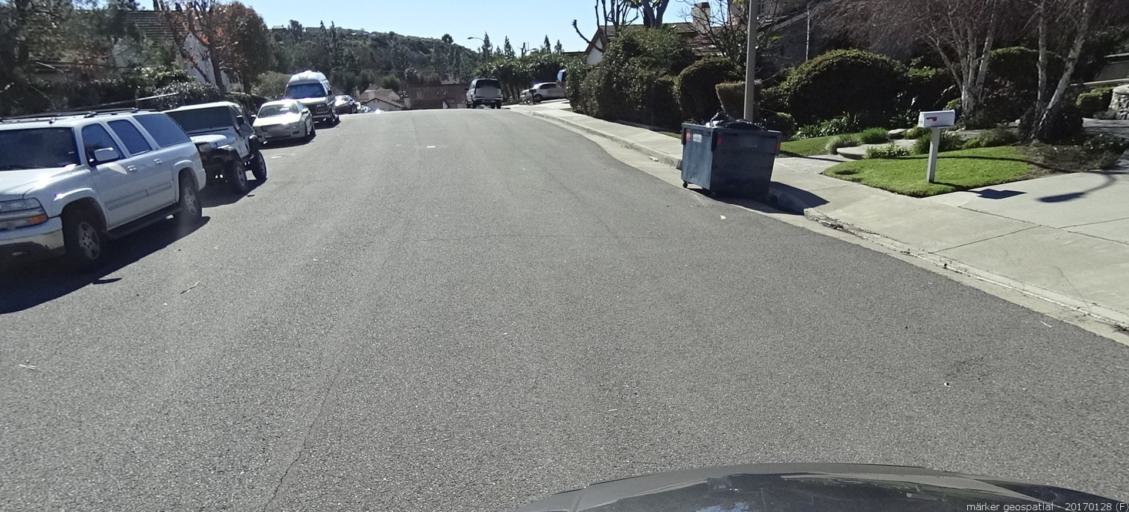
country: US
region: California
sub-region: Orange County
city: Lake Forest
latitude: 33.6591
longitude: -117.6769
